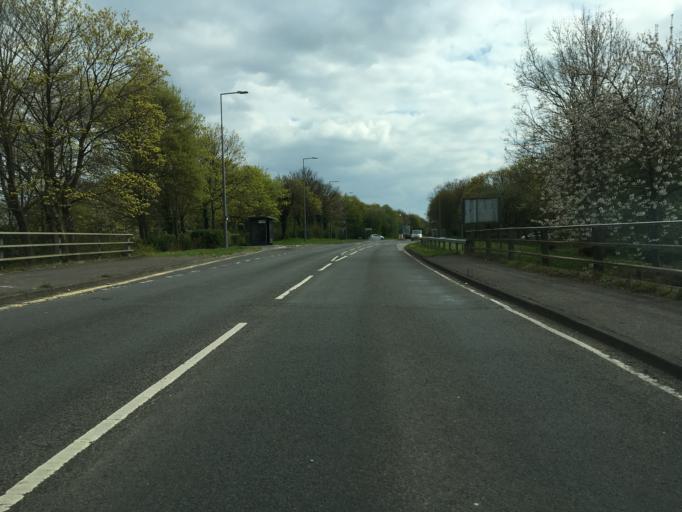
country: GB
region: England
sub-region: Milton Keynes
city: Milton Keynes
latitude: 52.0654
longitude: -0.7602
